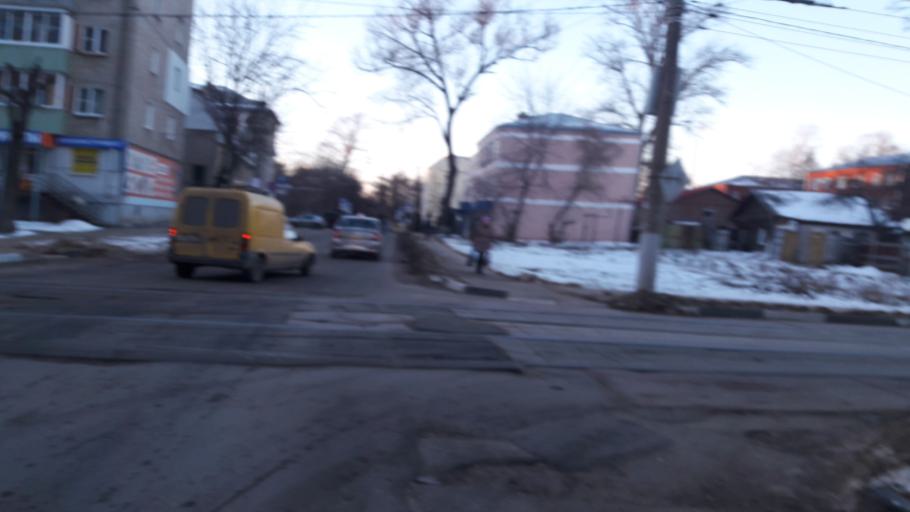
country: RU
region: Tula
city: Tula
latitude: 54.1846
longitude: 37.6044
